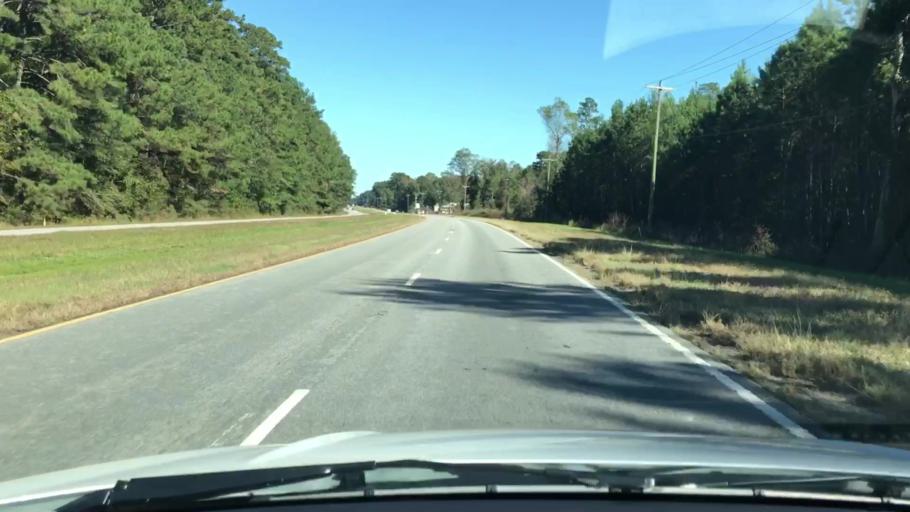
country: US
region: South Carolina
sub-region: Charleston County
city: Ravenel
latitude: 32.7553
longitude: -80.3287
